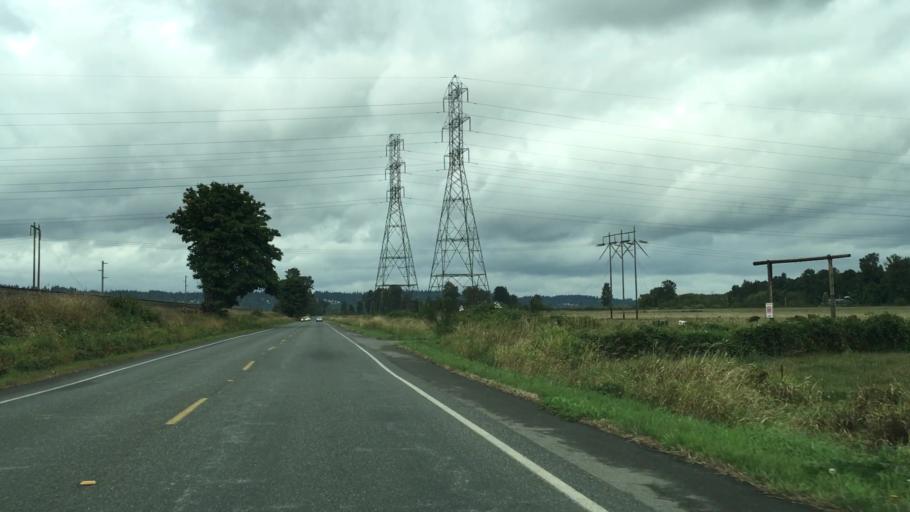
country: US
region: Washington
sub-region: Snohomish County
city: Fobes Hill
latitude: 47.9169
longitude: -122.1344
